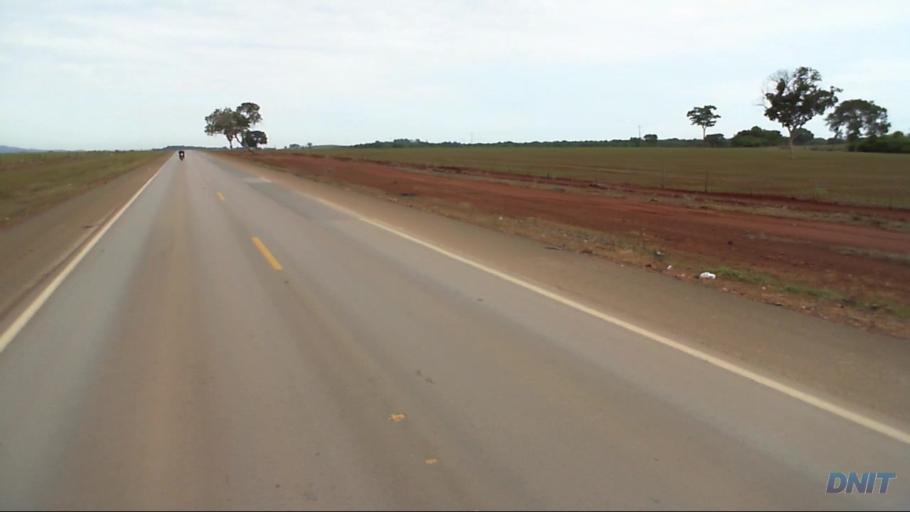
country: BR
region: Goias
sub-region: Uruacu
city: Uruacu
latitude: -14.7015
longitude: -49.1175
